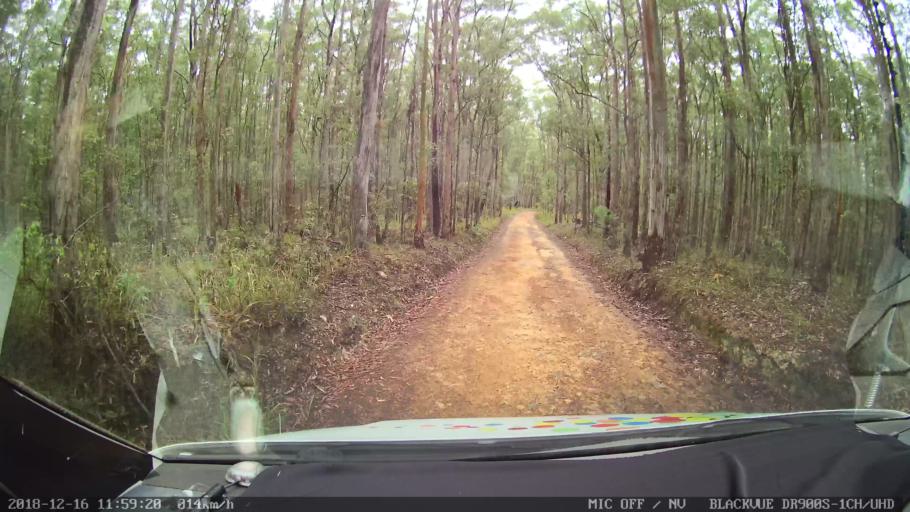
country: AU
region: New South Wales
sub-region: Tenterfield Municipality
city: Carrolls Creek
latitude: -28.9263
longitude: 152.3161
